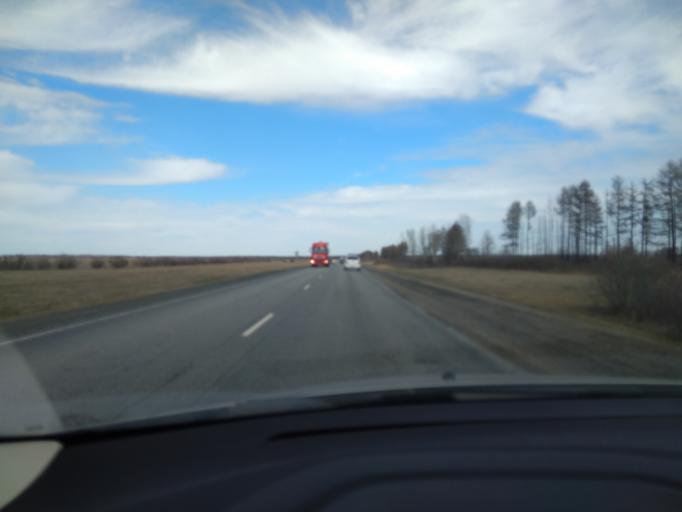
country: RU
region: Sverdlovsk
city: Pyshma
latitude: 57.0303
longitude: 63.4120
